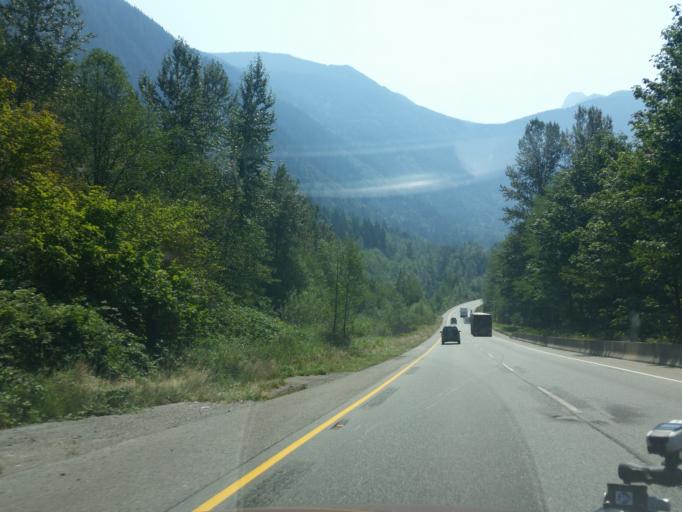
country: CA
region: British Columbia
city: Agassiz
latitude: 49.2521
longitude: -121.6814
